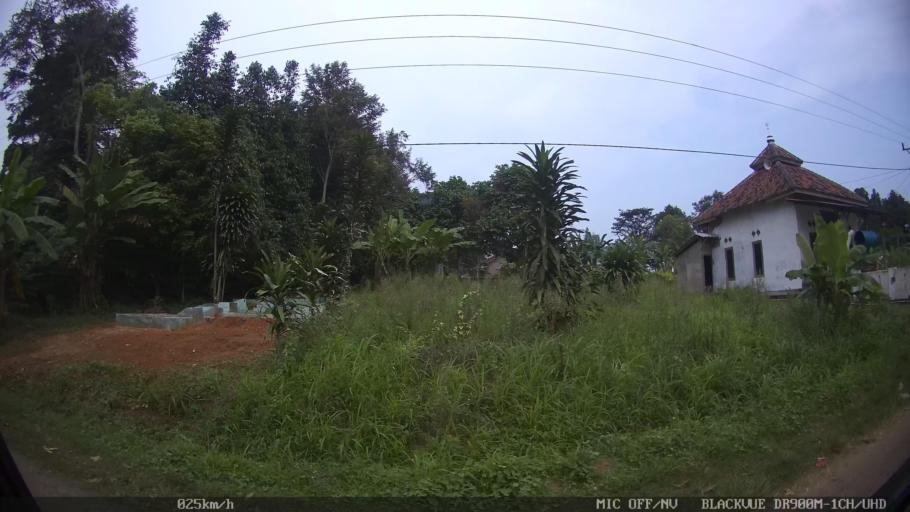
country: ID
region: Lampung
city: Panjang
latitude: -5.4159
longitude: 105.3571
